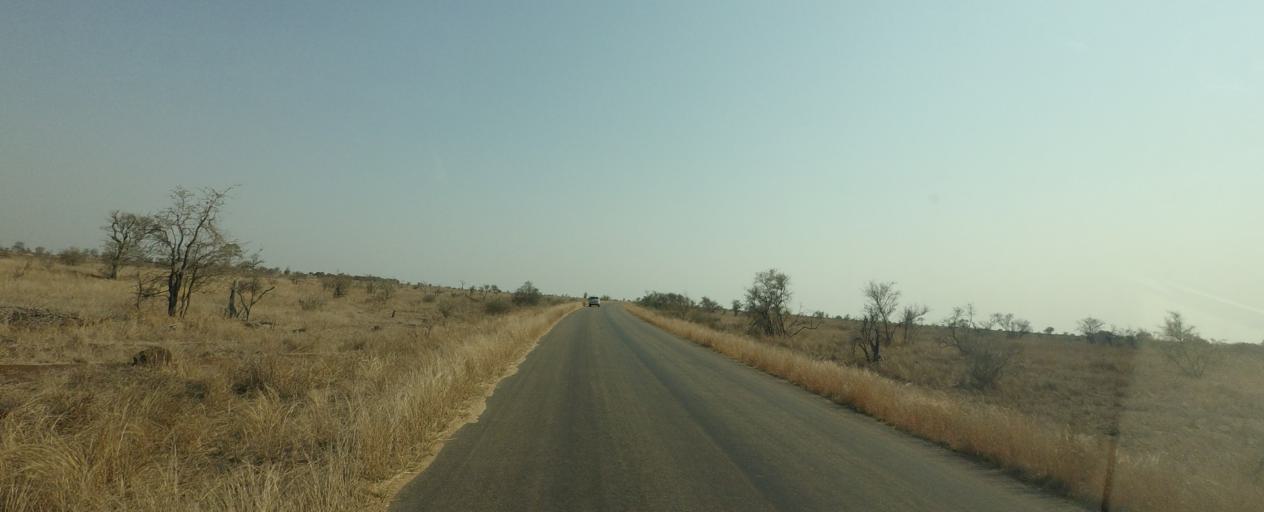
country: ZA
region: Limpopo
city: Thulamahashi
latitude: -24.3621
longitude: 31.7635
